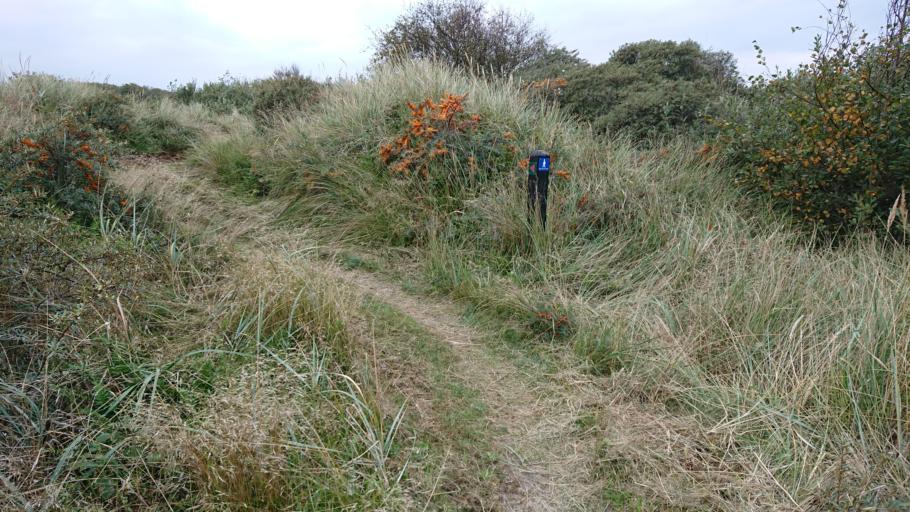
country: DK
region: North Denmark
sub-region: Frederikshavn Kommune
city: Skagen
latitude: 57.7467
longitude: 10.6268
